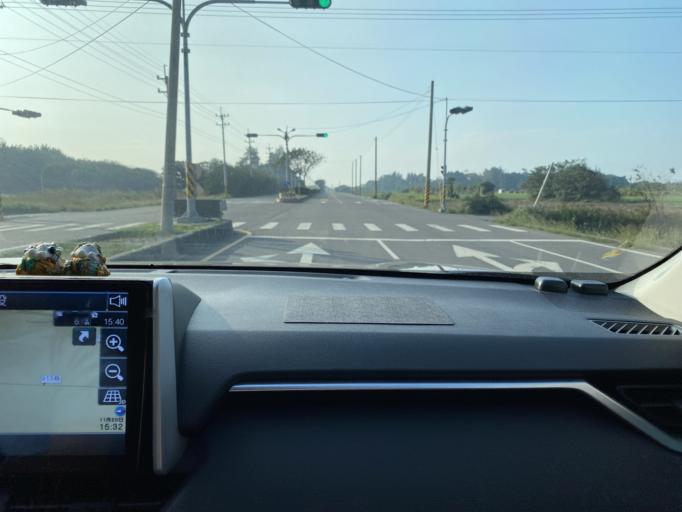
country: TW
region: Taiwan
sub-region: Changhua
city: Chang-hua
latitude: 23.9597
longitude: 120.3973
